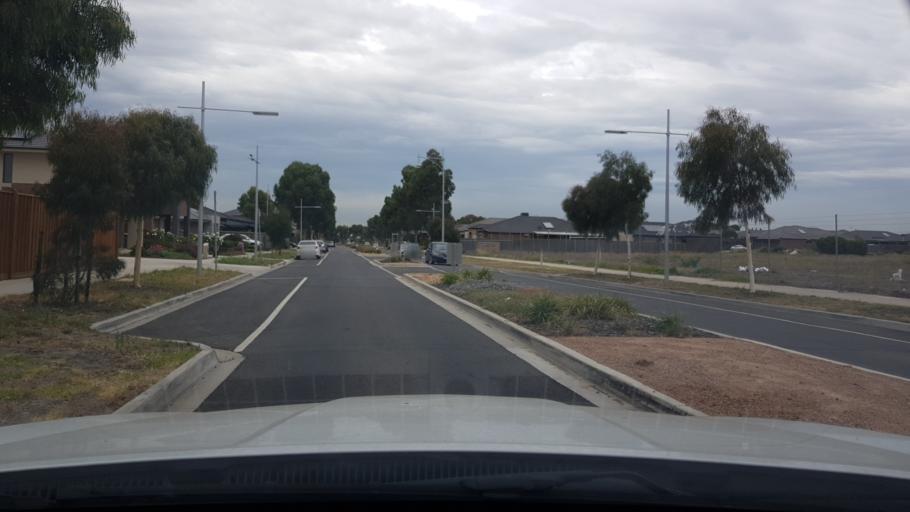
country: AU
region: Victoria
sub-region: Whittlesea
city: Lalor
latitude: -37.6583
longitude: 144.9972
